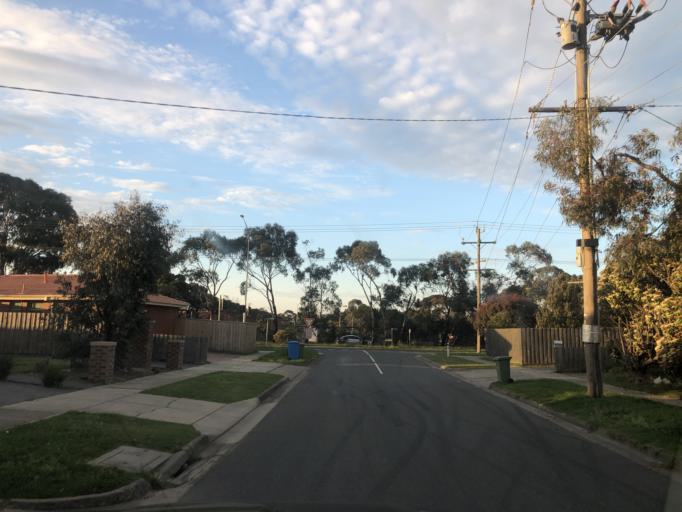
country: AU
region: Victoria
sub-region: Casey
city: Hampton Park
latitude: -38.0280
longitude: 145.2611
